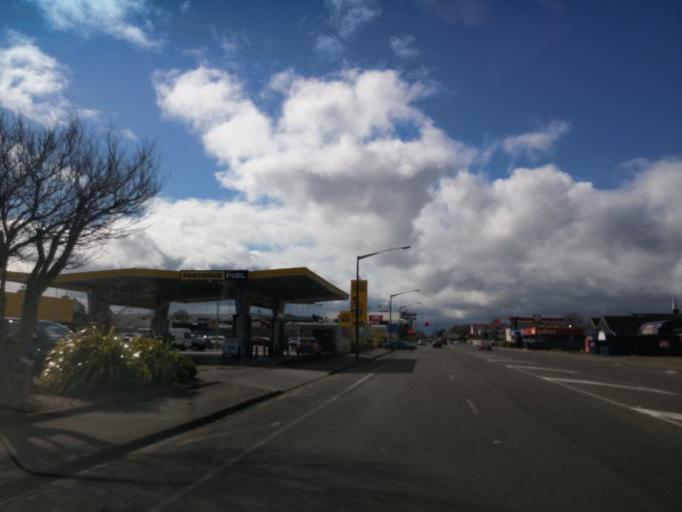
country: NZ
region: Manawatu-Wanganui
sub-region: Palmerston North City
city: Palmerston North
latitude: -40.3602
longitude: 175.6115
